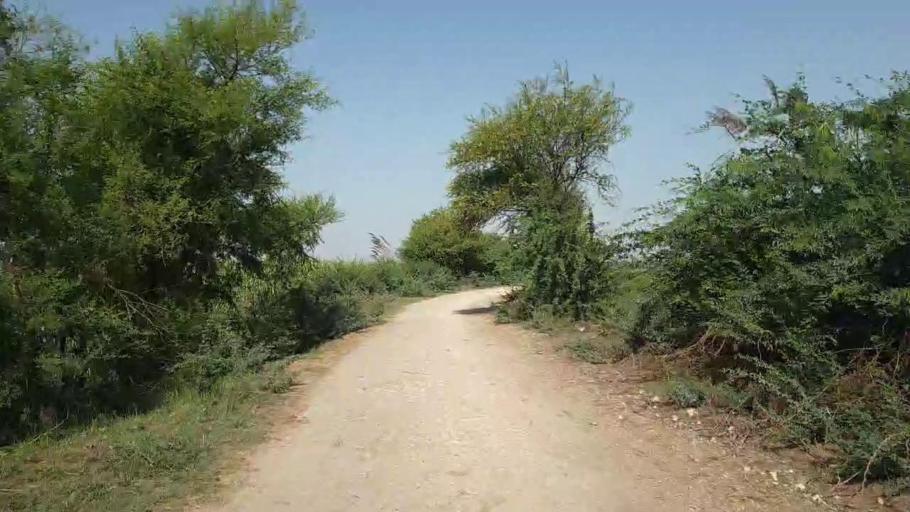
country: PK
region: Sindh
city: Tando Bago
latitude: 24.7582
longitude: 69.0245
